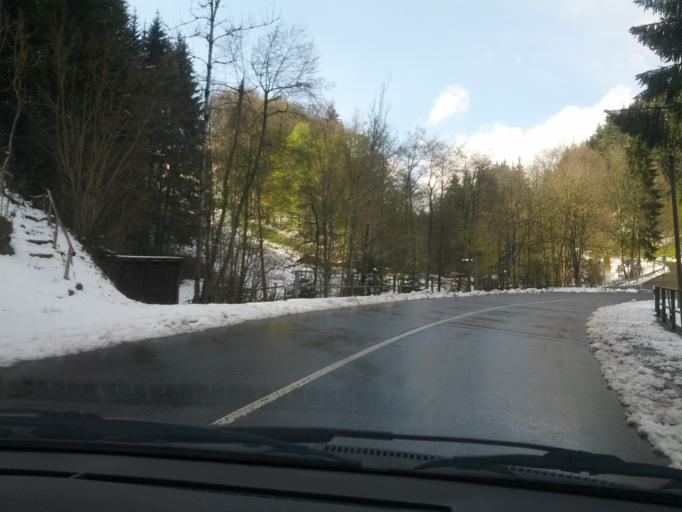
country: DE
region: Baden-Wuerttemberg
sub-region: Freiburg Region
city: Sankt Peter
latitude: 48.0275
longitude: 8.0259
